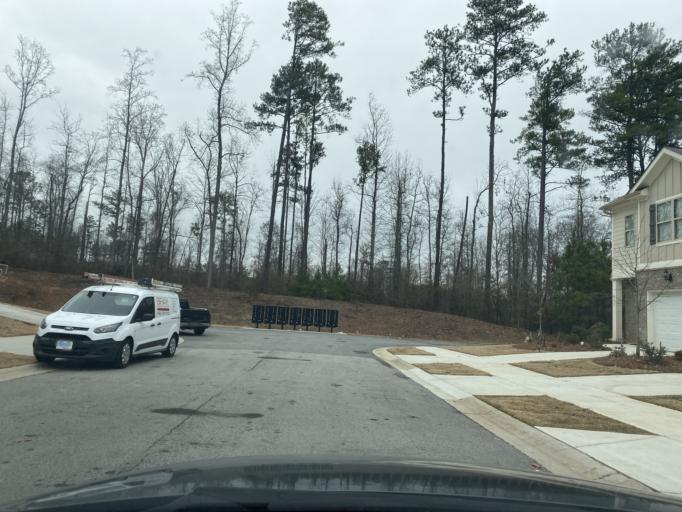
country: US
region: Georgia
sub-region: DeKalb County
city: Pine Mountain
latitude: 33.6912
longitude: -84.1556
